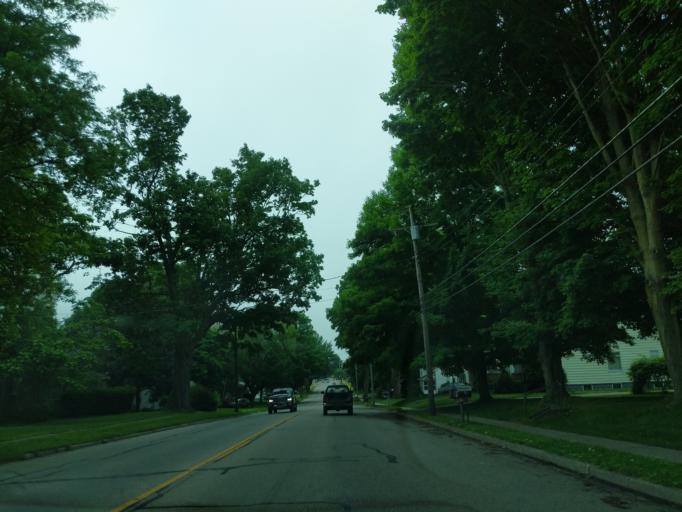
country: US
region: Michigan
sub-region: Hillsdale County
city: Litchfield
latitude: 42.0471
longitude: -84.7623
